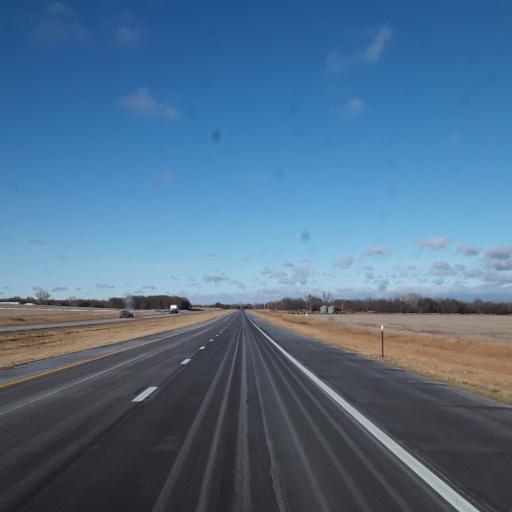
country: US
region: Kansas
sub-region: Republic County
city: Belleville
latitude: 39.7146
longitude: -97.6603
